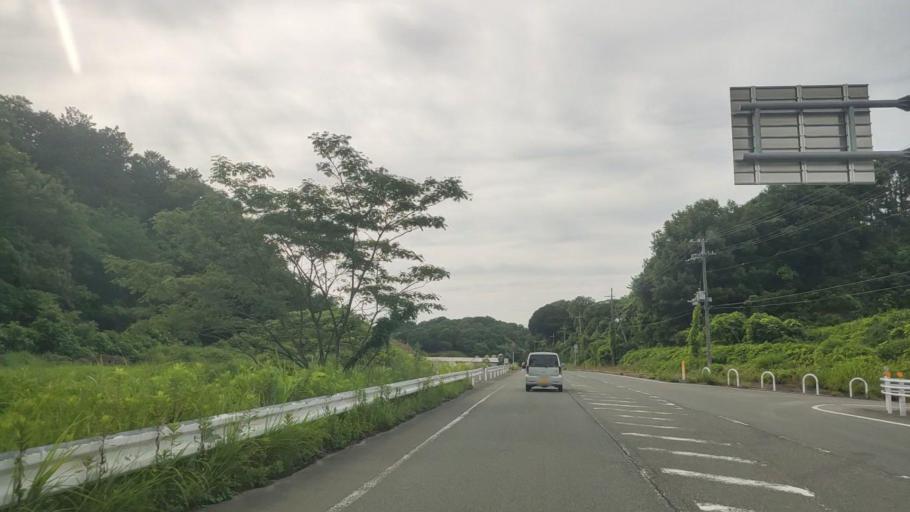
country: JP
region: Kyoto
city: Miyazu
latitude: 35.6778
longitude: 135.0708
